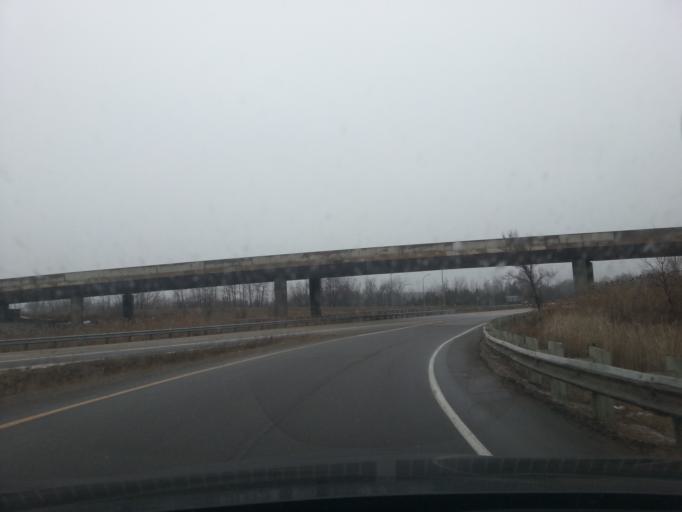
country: CA
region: Ontario
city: Omemee
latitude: 44.2034
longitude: -78.4464
